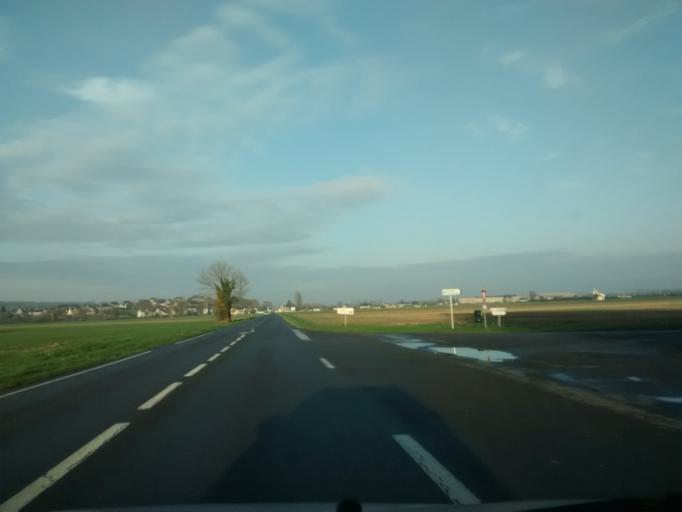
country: FR
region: Lower Normandy
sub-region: Departement de la Manche
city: Pontorson
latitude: 48.5639
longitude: -1.5368
